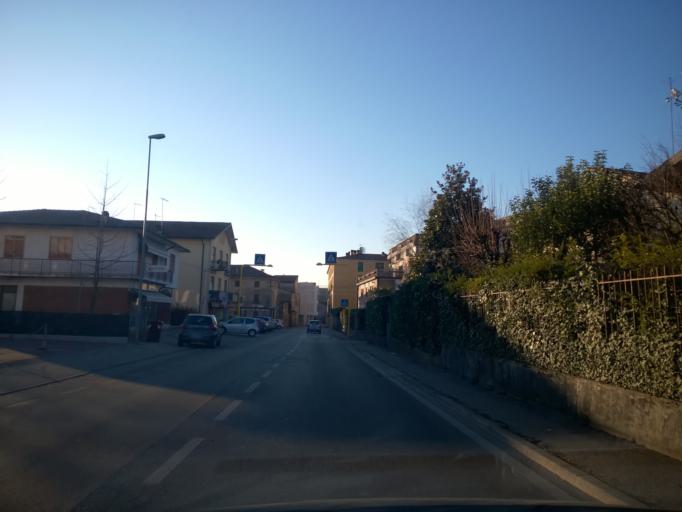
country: IT
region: Veneto
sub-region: Provincia di Vicenza
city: Thiene
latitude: 45.7126
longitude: 11.4695
